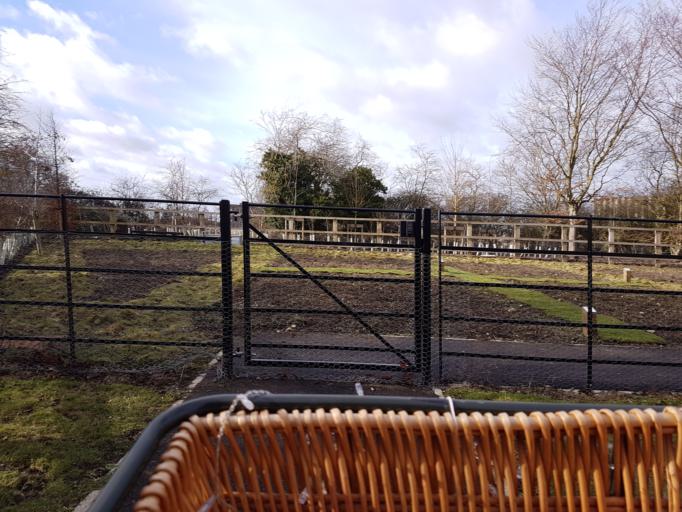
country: GB
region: England
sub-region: Cambridgeshire
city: Cambridge
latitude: 52.1710
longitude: 0.1418
